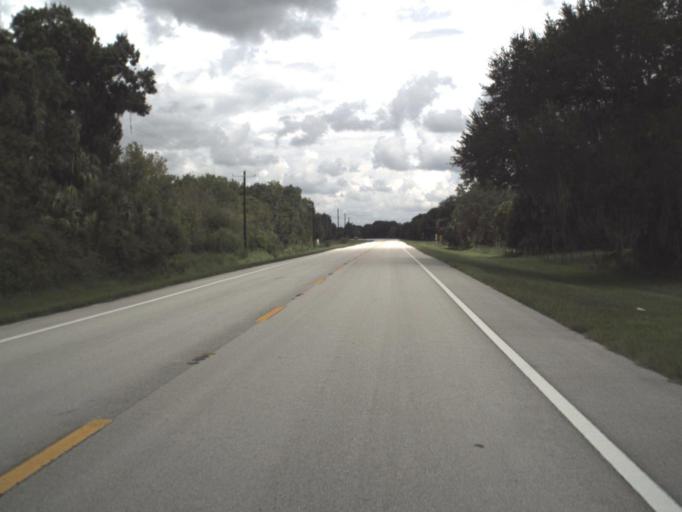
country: US
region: Florida
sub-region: DeSoto County
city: Nocatee
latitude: 27.2032
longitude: -82.0491
